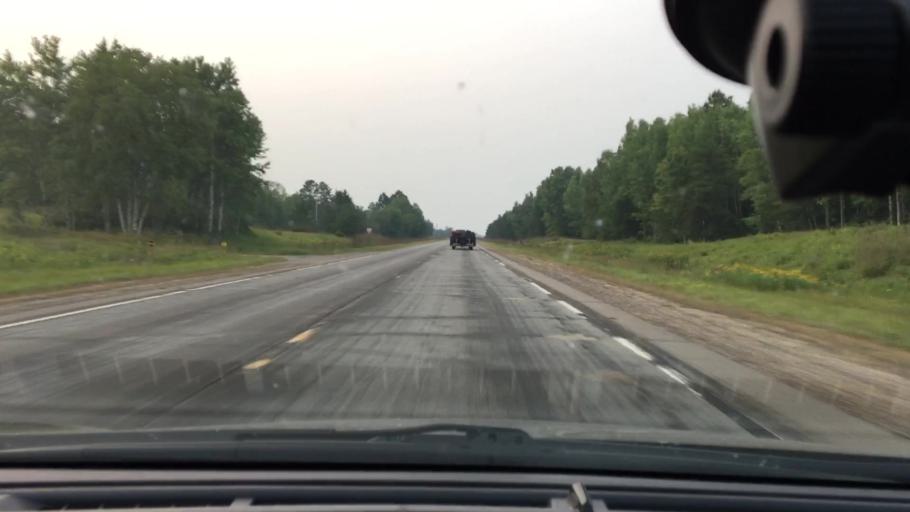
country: US
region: Minnesota
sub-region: Crow Wing County
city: Cross Lake
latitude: 46.6795
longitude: -93.9529
